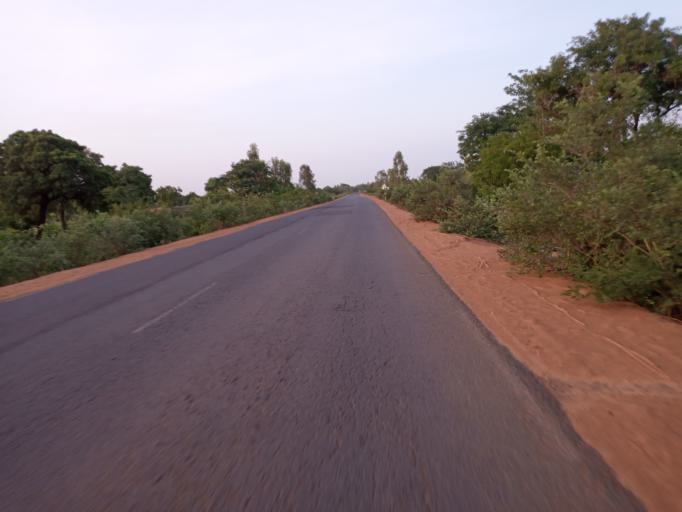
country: ML
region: Bamako
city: Bamako
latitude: 12.2931
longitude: -8.1667
